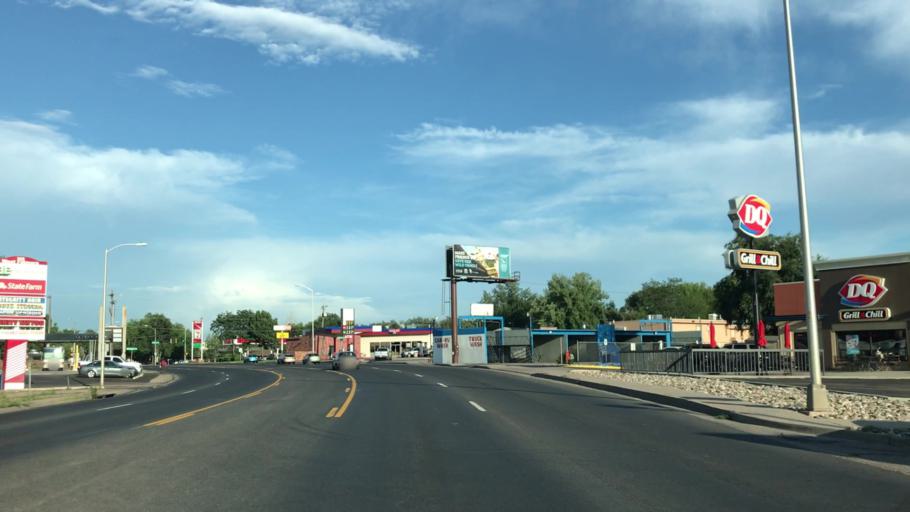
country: US
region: Colorado
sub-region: El Paso County
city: Colorado Springs
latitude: 38.8754
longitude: -104.8281
